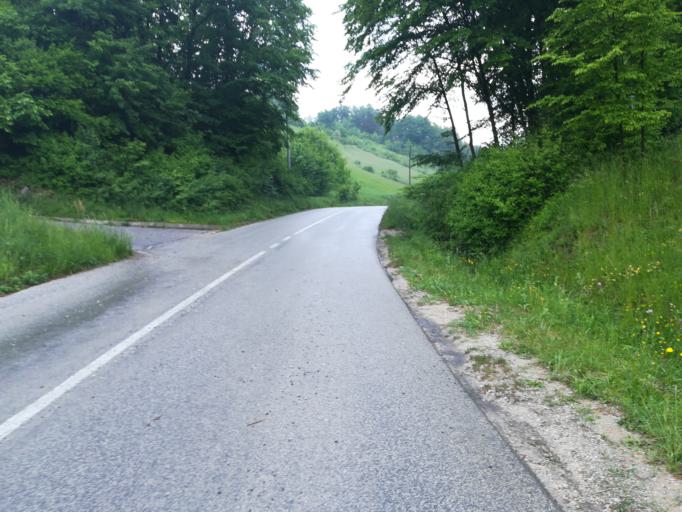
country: HR
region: Varazdinska
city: Klenovnik
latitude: 46.2954
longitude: 16.0208
